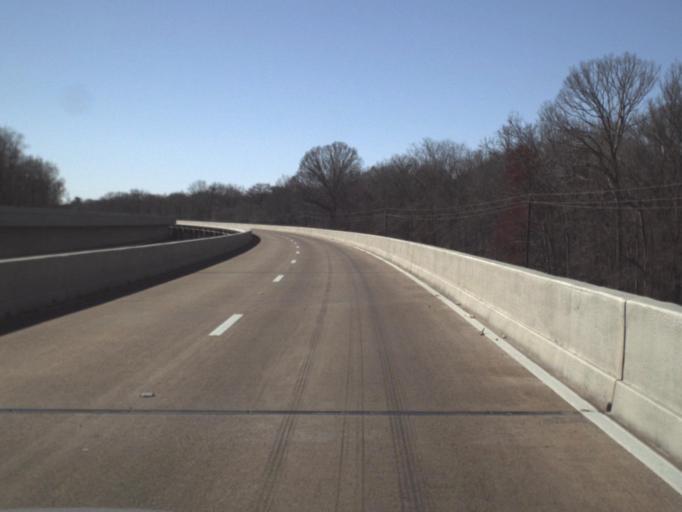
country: US
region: Florida
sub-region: Liberty County
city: Bristol
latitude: 30.4426
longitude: -85.0066
